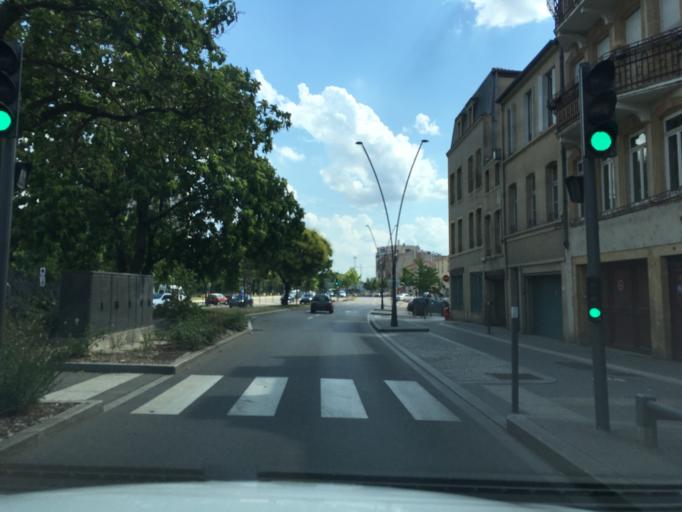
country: FR
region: Lorraine
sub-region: Departement de la Moselle
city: Metz
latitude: 49.1175
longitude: 6.1850
